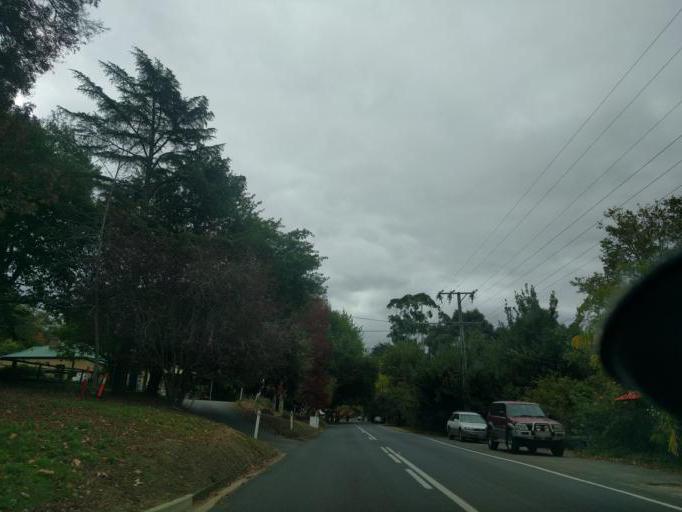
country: AU
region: South Australia
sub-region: Adelaide Hills
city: Stirling
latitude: -35.0441
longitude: 138.7598
